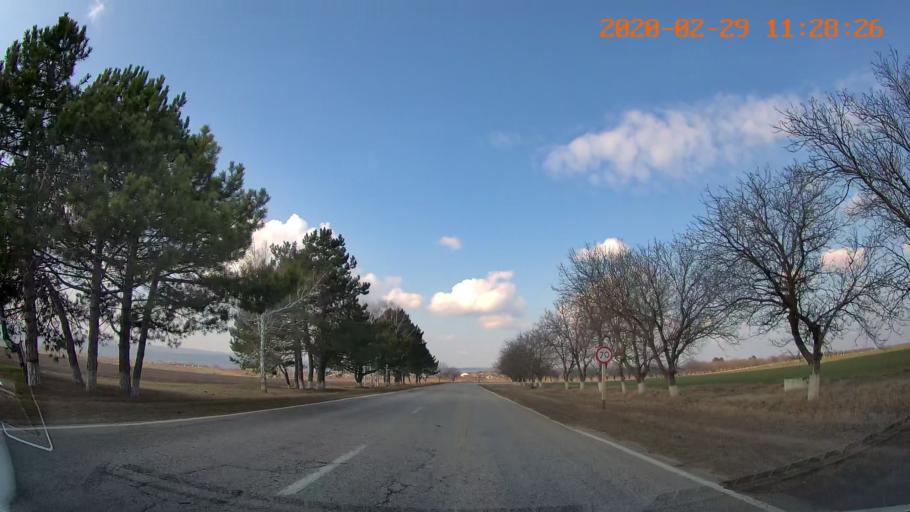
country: MD
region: Telenesti
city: Cocieri
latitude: 47.4813
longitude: 29.1355
